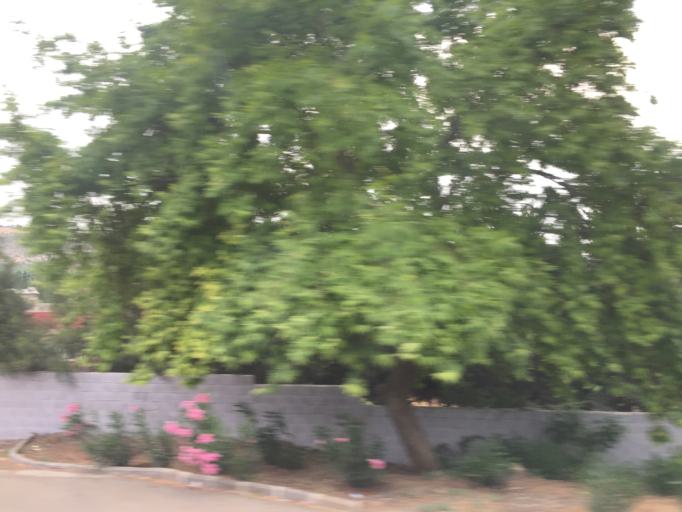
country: TR
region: Gaziantep
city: Gaziantep
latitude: 37.0070
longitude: 37.4316
